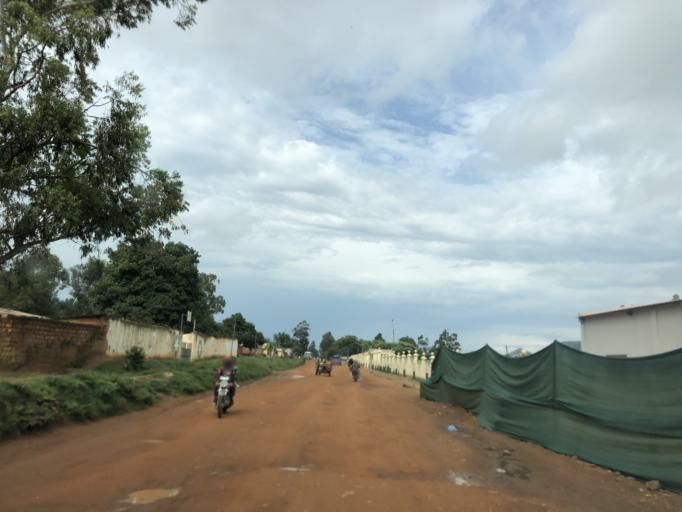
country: AO
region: Cuanza Sul
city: Uacu Cungo
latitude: -11.3481
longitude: 15.1009
